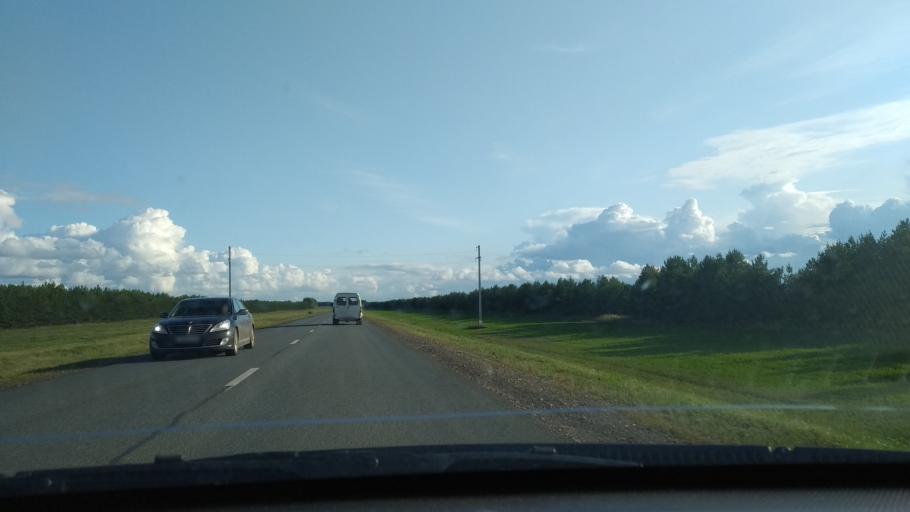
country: RU
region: Tatarstan
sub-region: Alekseyevskiy Rayon
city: Alekseyevskoye
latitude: 55.2256
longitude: 50.1024
